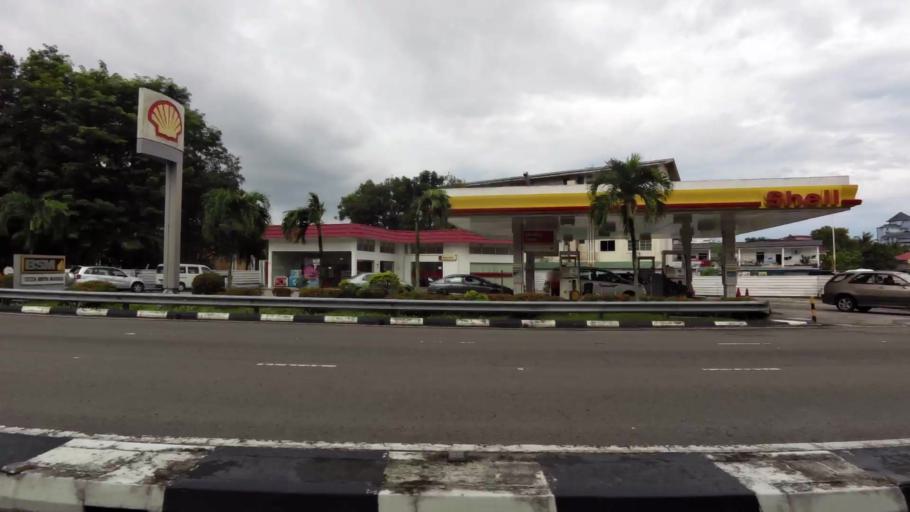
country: BN
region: Brunei and Muara
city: Bandar Seri Begawan
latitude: 4.9023
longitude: 114.9396
